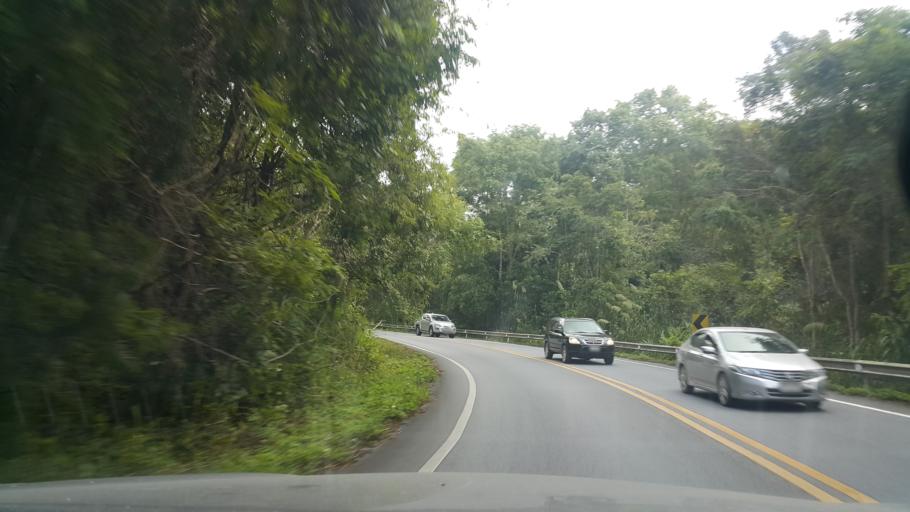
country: TH
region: Lampang
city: Wang Nuea
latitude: 19.0630
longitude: 99.7532
